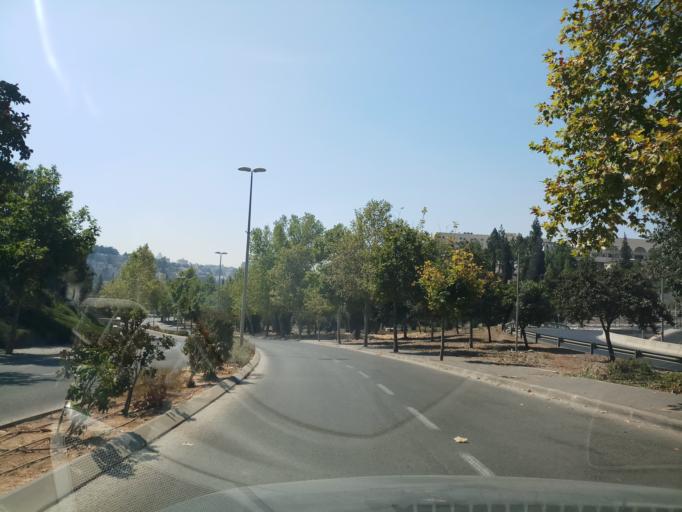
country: IL
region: Jerusalem
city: Jerusalem
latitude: 31.7679
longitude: 35.1959
